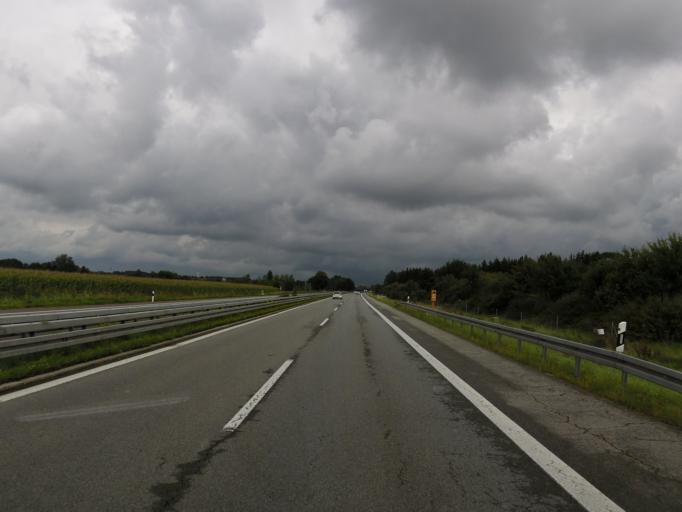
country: DE
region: Bavaria
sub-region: Swabia
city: Wiedergeltingen
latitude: 48.0276
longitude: 10.6796
